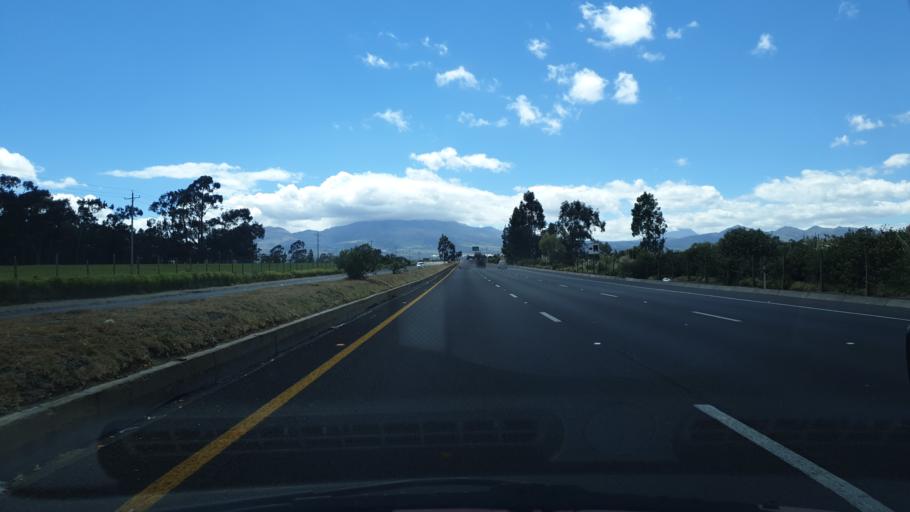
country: EC
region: Cotopaxi
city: Saquisili
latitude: -0.8233
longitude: -78.6222
